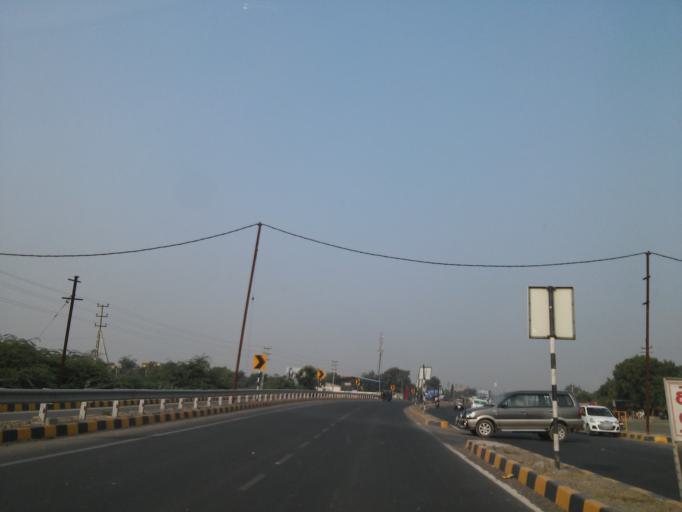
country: IN
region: Gujarat
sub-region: Kachchh
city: Bhuj
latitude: 23.2366
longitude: 69.7258
